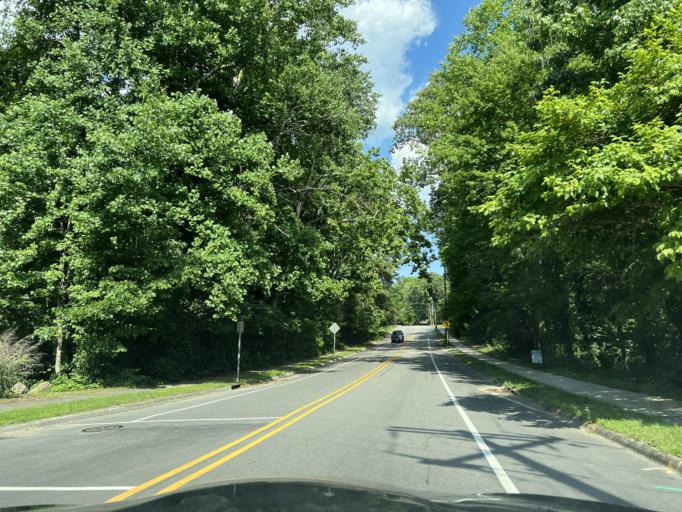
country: US
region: North Carolina
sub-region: Durham County
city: Durham
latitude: 36.0288
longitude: -78.8983
